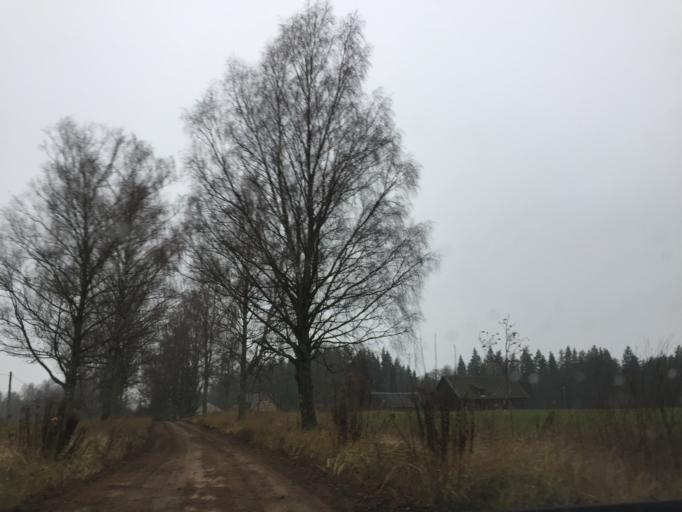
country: LV
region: Koceni
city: Koceni
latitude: 57.5092
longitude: 25.3172
